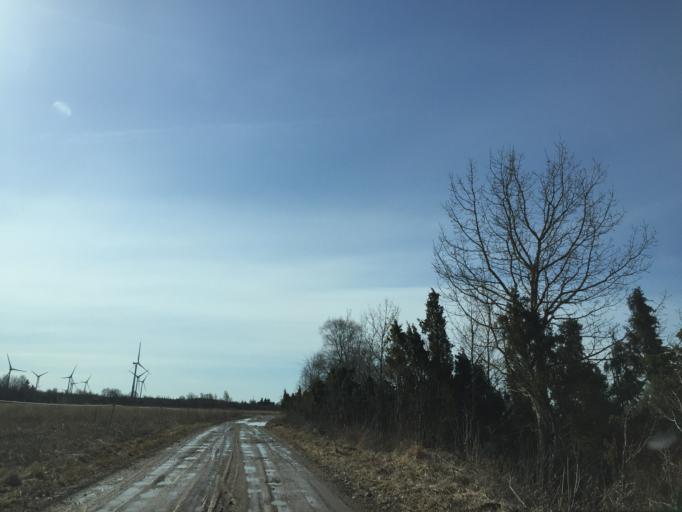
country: EE
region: Laeaene
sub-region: Haapsalu linn
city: Haapsalu
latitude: 58.6526
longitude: 23.5135
